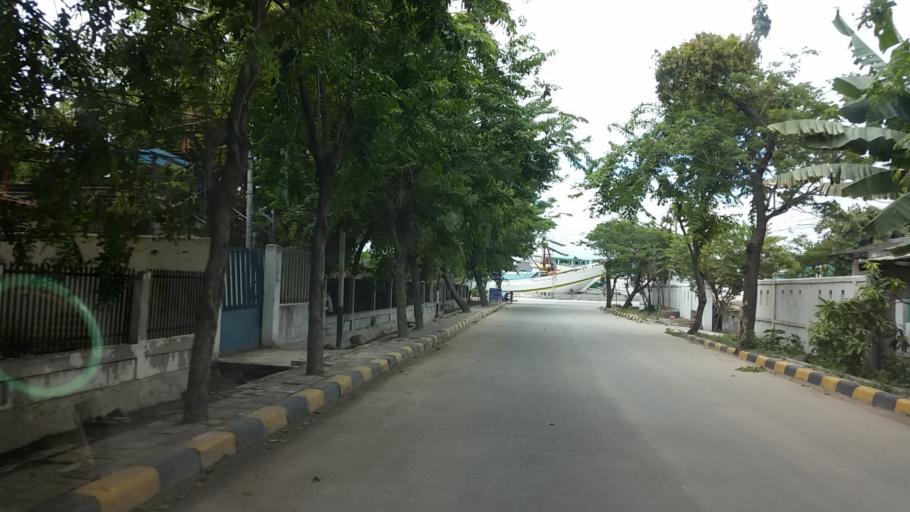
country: ID
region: Jakarta Raya
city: Jakarta
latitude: -6.1243
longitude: 106.8104
